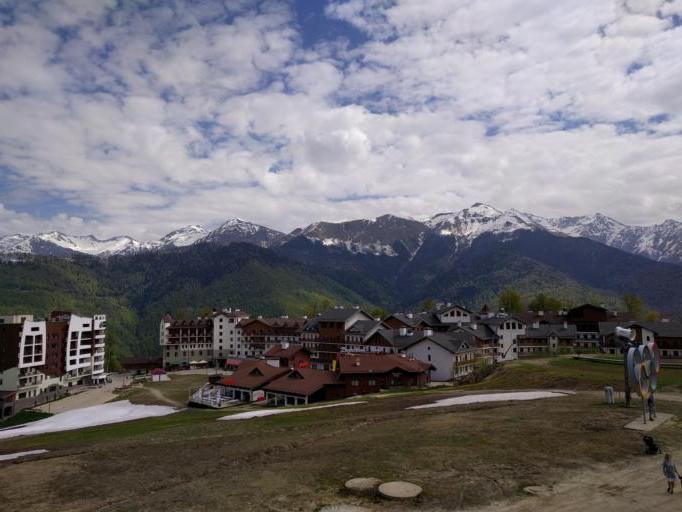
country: RU
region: Krasnodarskiy
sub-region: Sochi City
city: Krasnaya Polyana
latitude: 43.6589
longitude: 40.3184
